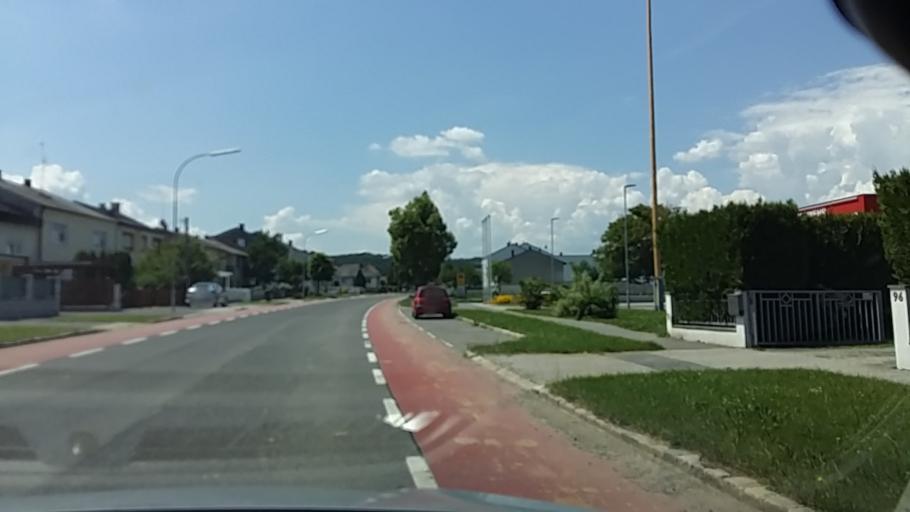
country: AT
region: Burgenland
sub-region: Politischer Bezirk Oberpullendorf
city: Piringsdorf
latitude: 47.4495
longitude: 16.4221
